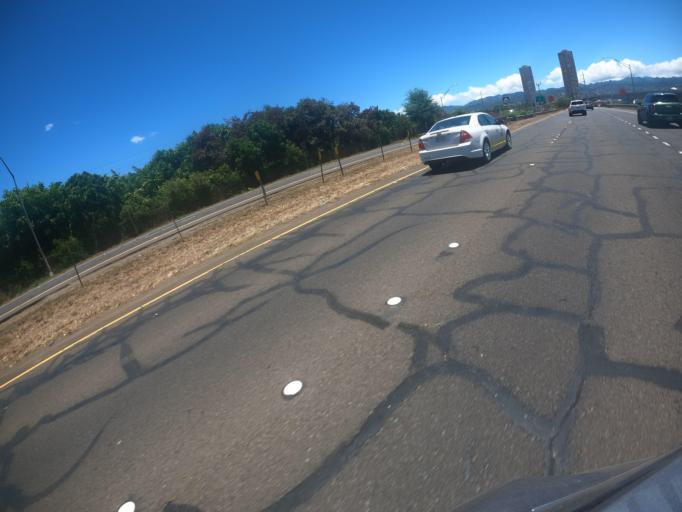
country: US
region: Hawaii
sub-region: Honolulu County
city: Pearl City, Manana
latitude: 21.3958
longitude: -157.9863
